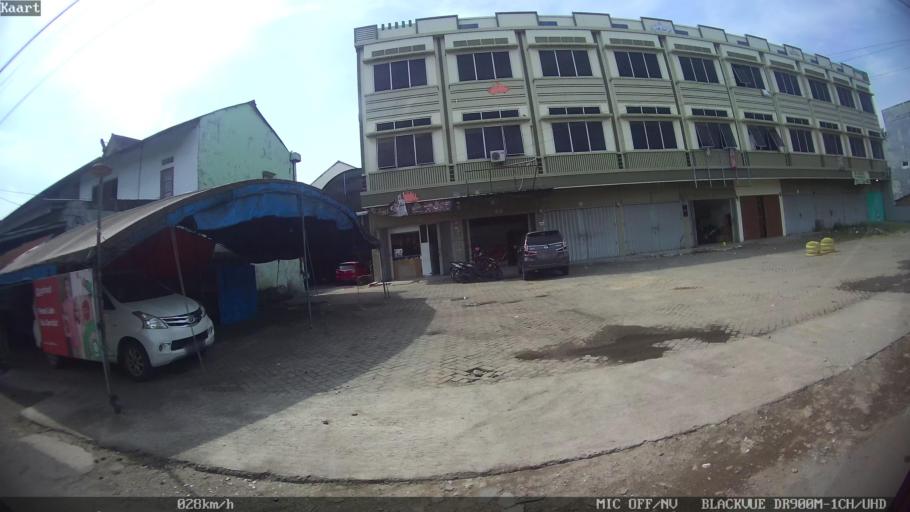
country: ID
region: Lampung
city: Kedaton
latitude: -5.3883
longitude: 105.2902
